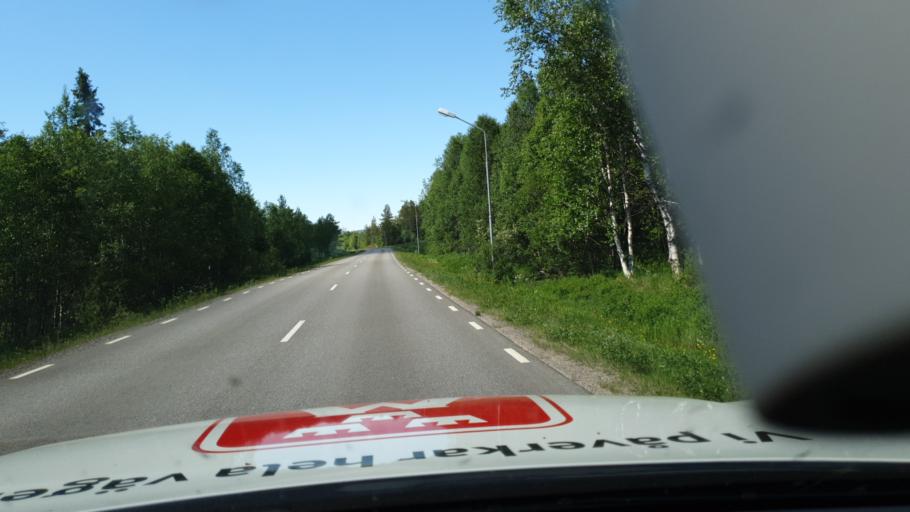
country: SE
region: Jaemtland
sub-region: Harjedalens Kommun
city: Sveg
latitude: 62.1043
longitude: 13.4909
